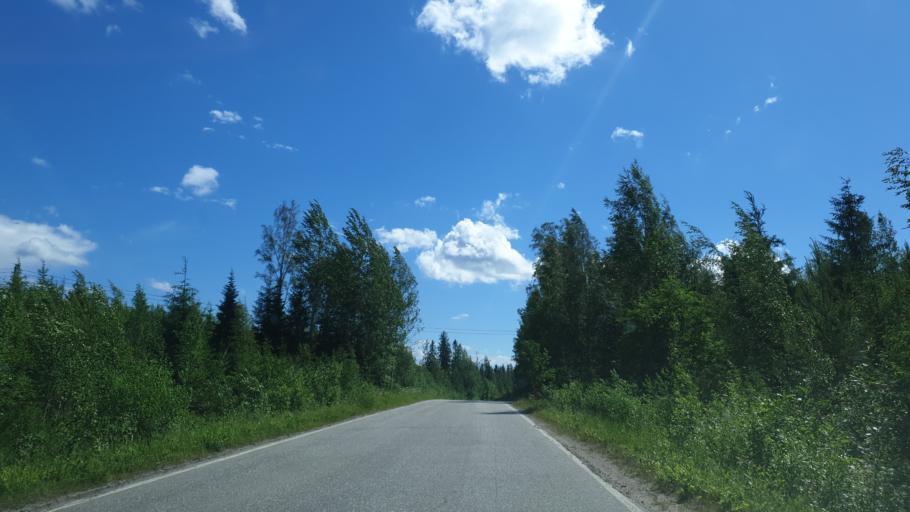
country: FI
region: Northern Savo
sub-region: Koillis-Savo
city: Kaavi
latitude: 62.9976
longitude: 28.5034
